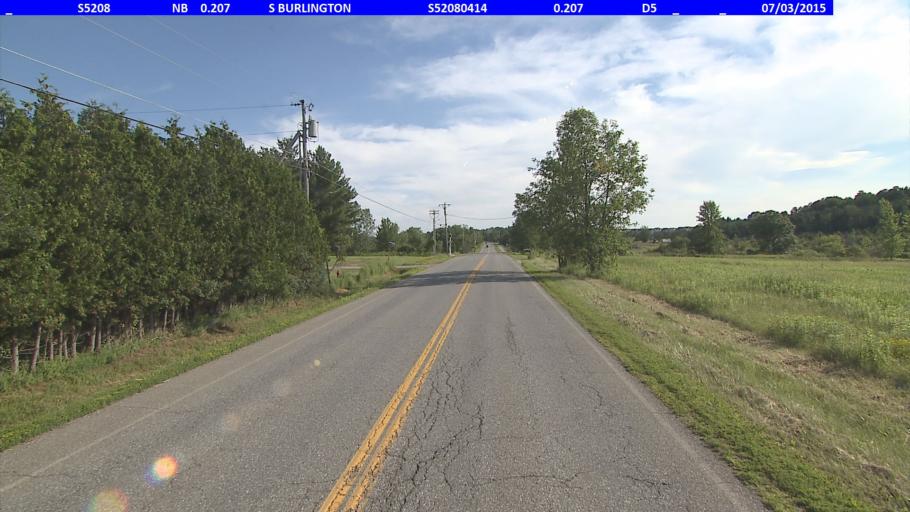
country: US
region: Vermont
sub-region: Chittenden County
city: South Burlington
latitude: 44.4141
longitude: -73.1755
